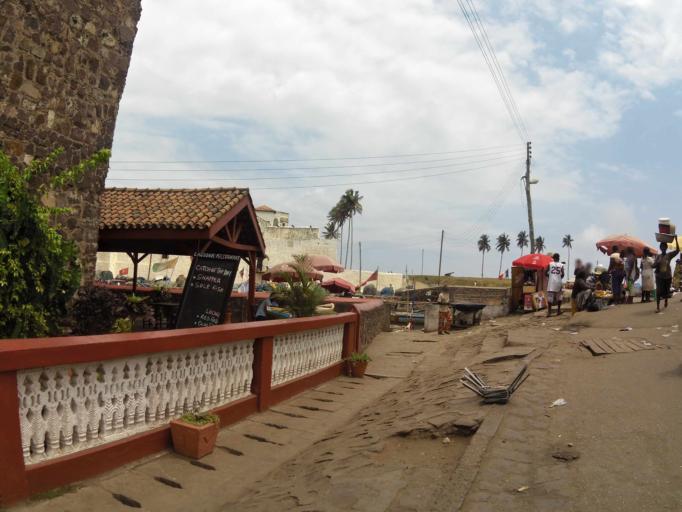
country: GH
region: Central
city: Elmina
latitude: 5.0835
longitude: -1.3493
